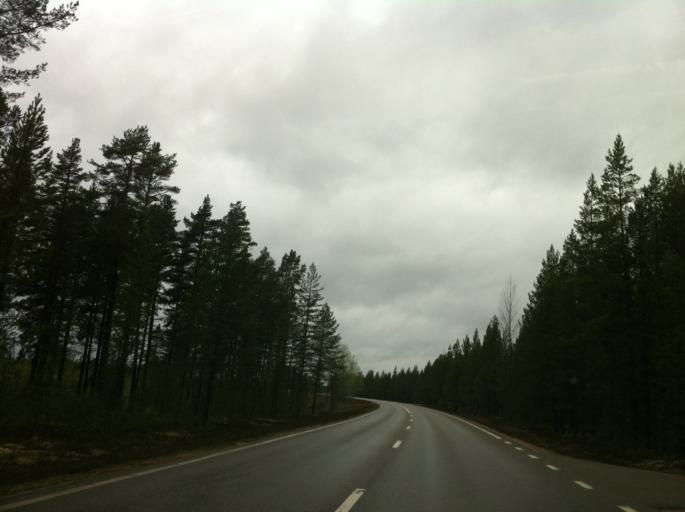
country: SE
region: Jaemtland
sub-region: Harjedalens Kommun
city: Sveg
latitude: 62.1359
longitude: 14.0440
